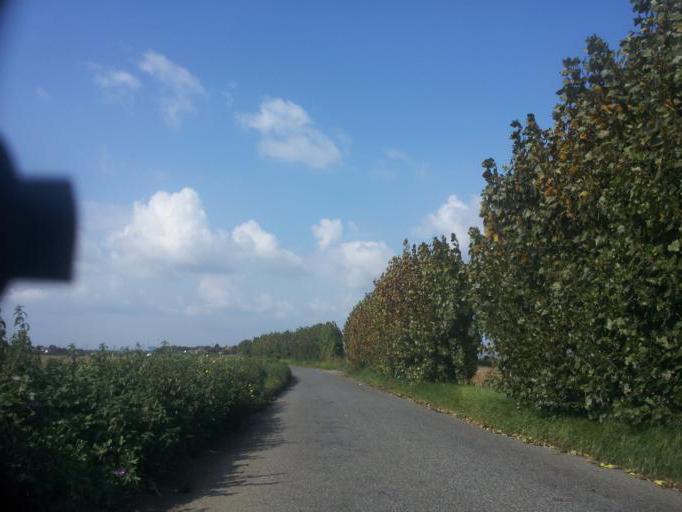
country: GB
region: England
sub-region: Kent
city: Strood
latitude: 51.4243
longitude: 0.4793
